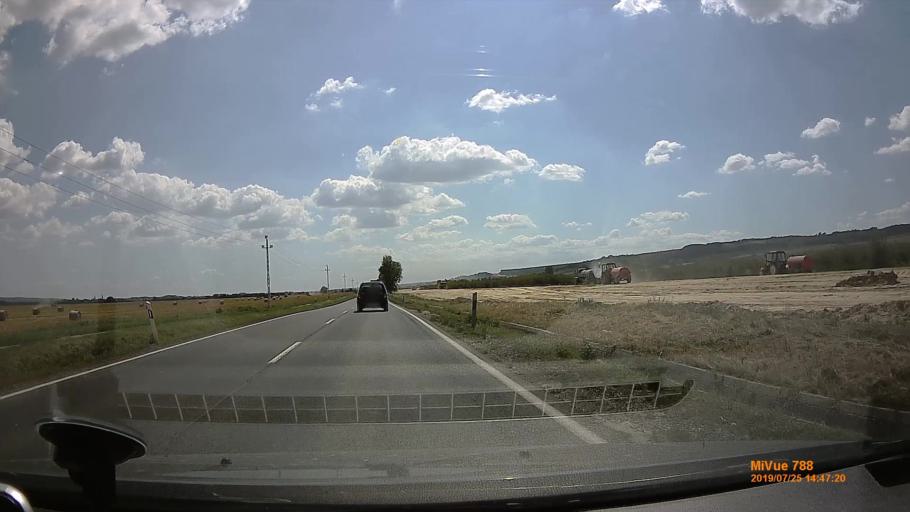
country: HU
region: Borsod-Abauj-Zemplen
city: Halmaj
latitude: 48.2479
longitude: 20.9756
